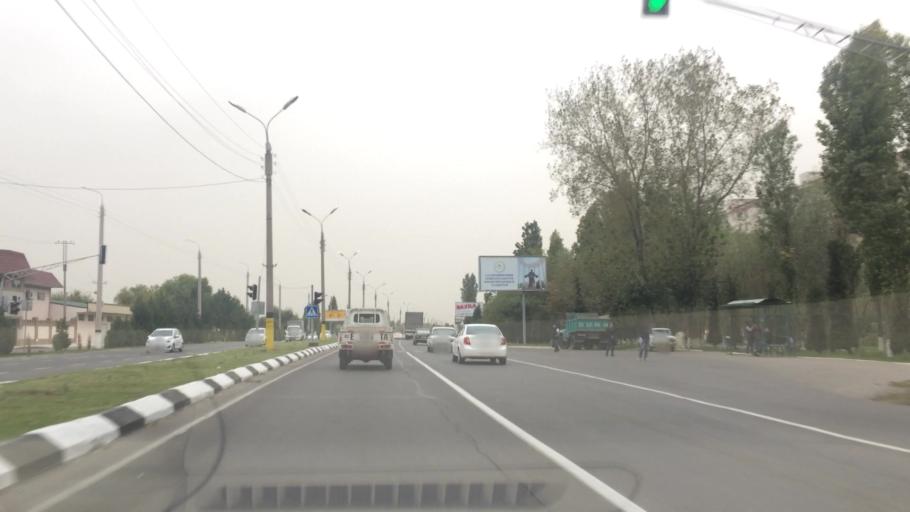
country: UZ
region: Toshkent
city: Salor
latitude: 41.3169
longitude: 69.3560
